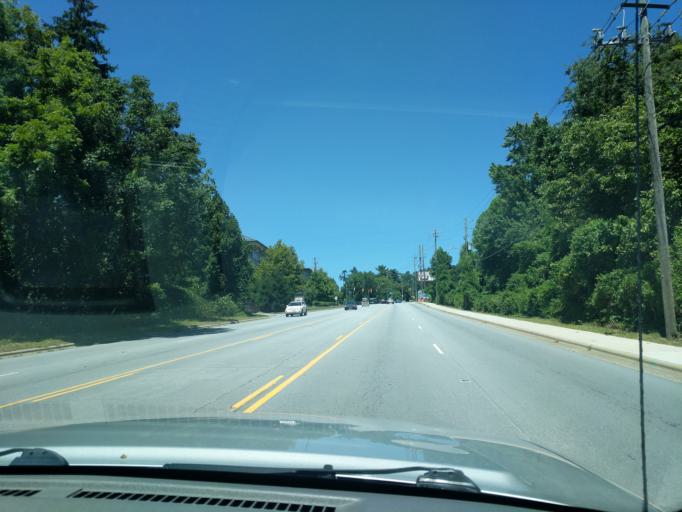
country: US
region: North Carolina
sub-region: Buncombe County
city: Biltmore Forest
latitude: 35.5320
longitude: -82.5282
